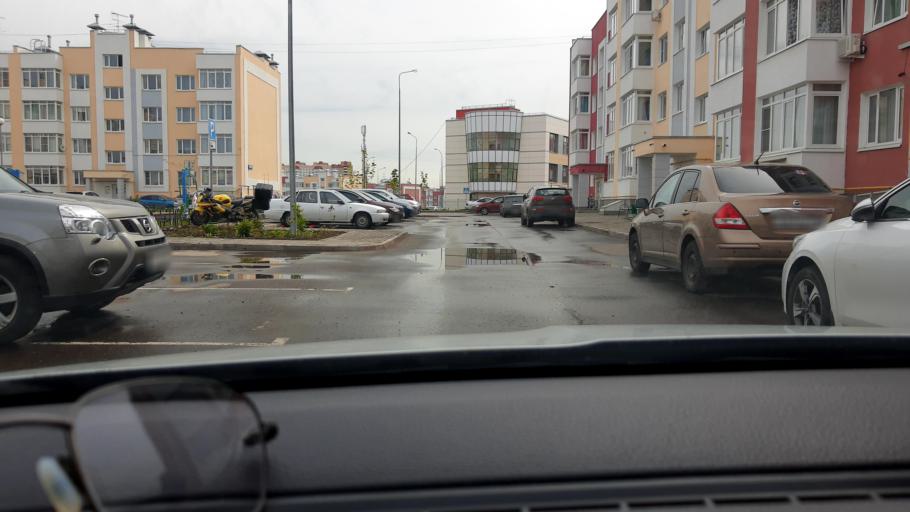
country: RU
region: Moskovskaya
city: Dedovsk
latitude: 55.8385
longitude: 37.1254
